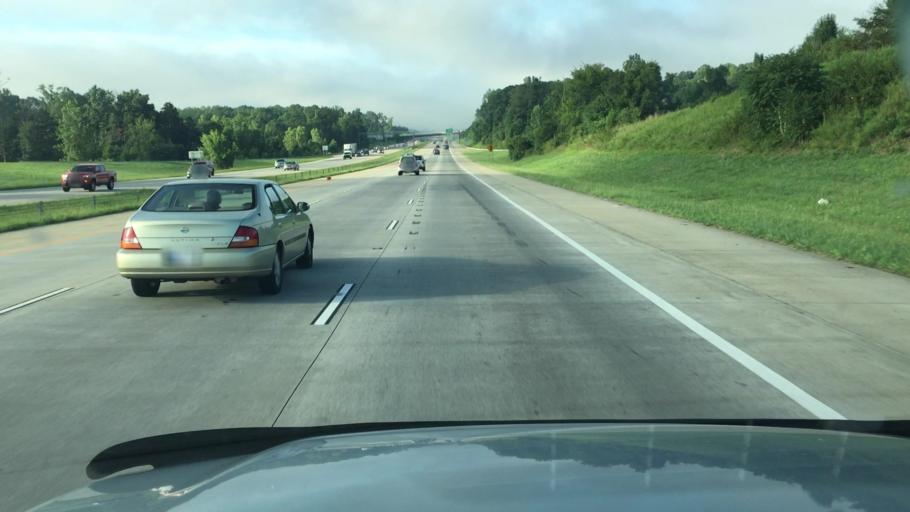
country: US
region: North Carolina
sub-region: Gaston County
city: Mount Holly
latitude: 35.2728
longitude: -80.9665
